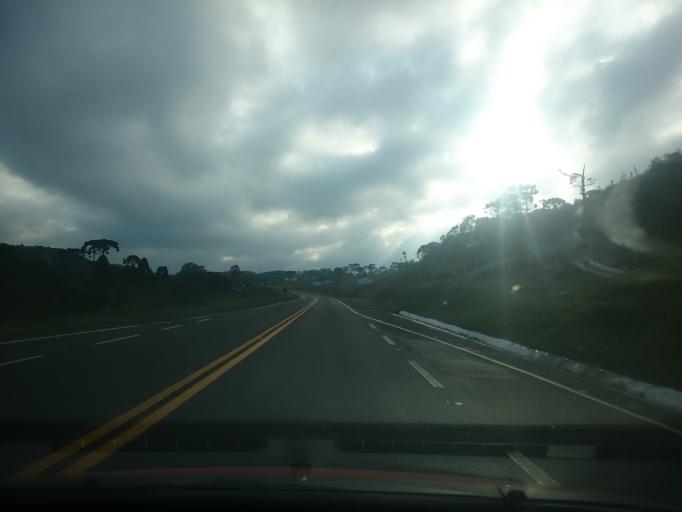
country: BR
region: Santa Catarina
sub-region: Lages
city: Lages
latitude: -27.9555
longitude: -50.4831
